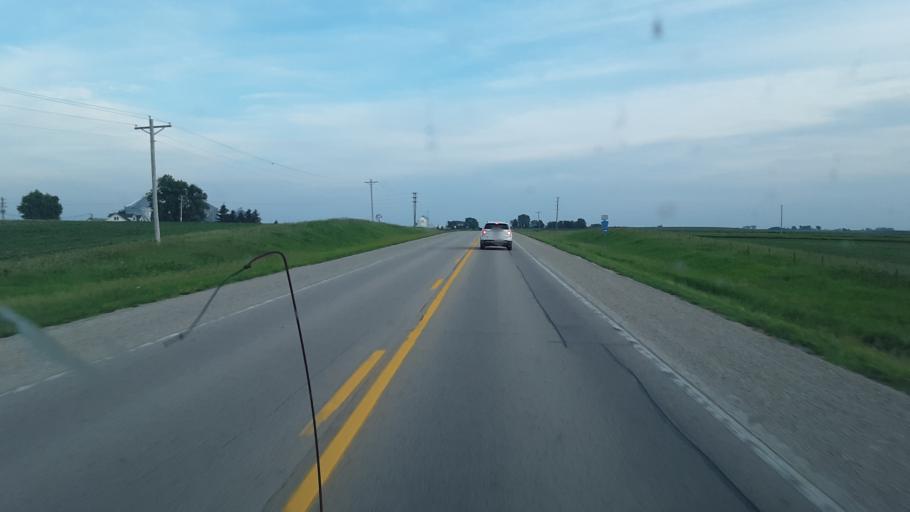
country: US
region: Iowa
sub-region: Benton County
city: Belle Plaine
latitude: 41.8001
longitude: -92.2789
